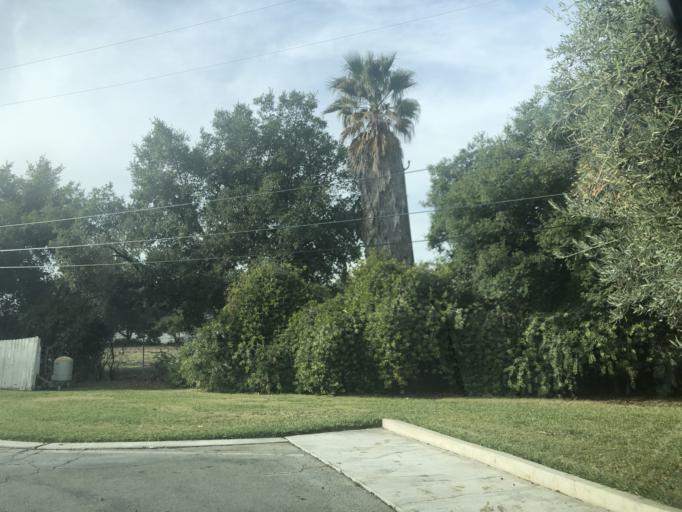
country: US
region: California
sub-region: Contra Costa County
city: Concord
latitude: 38.0054
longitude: -122.0395
